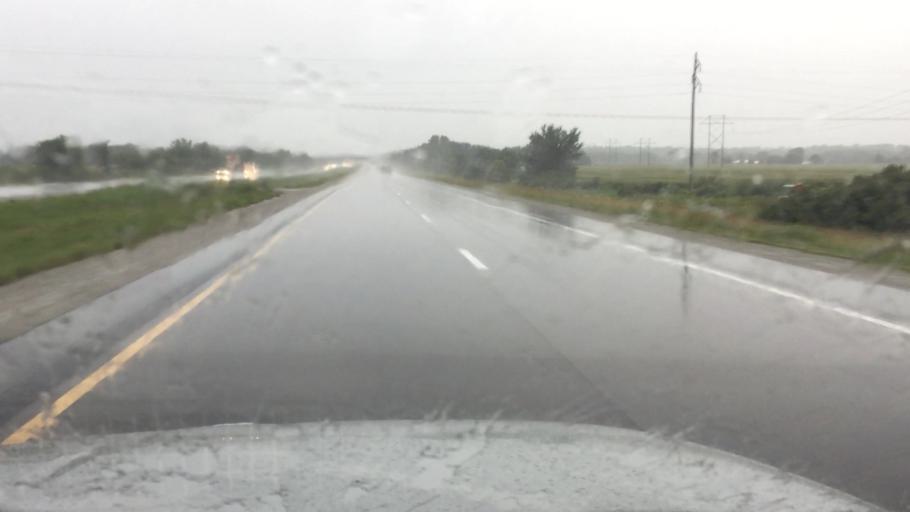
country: US
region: Iowa
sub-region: Johnson County
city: University Heights
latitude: 41.5700
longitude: -91.5453
